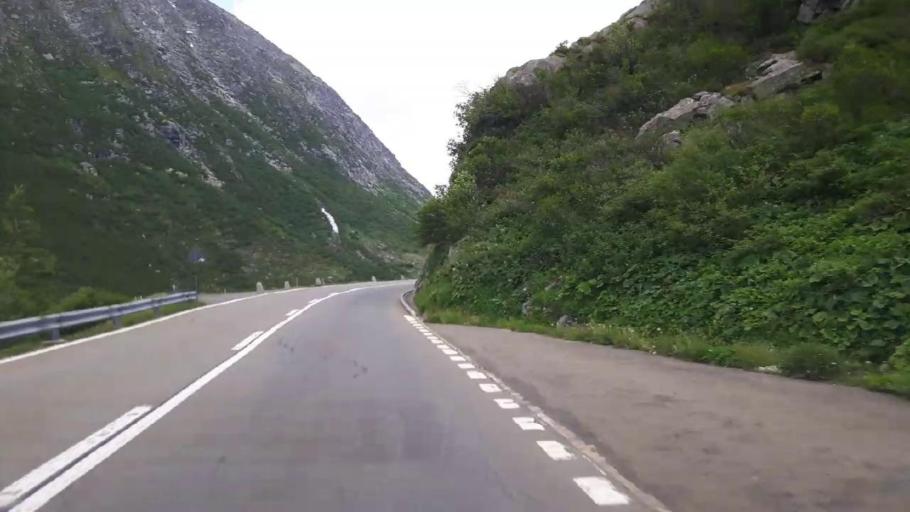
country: CH
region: Uri
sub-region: Uri
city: Andermatt
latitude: 46.5979
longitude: 8.5631
